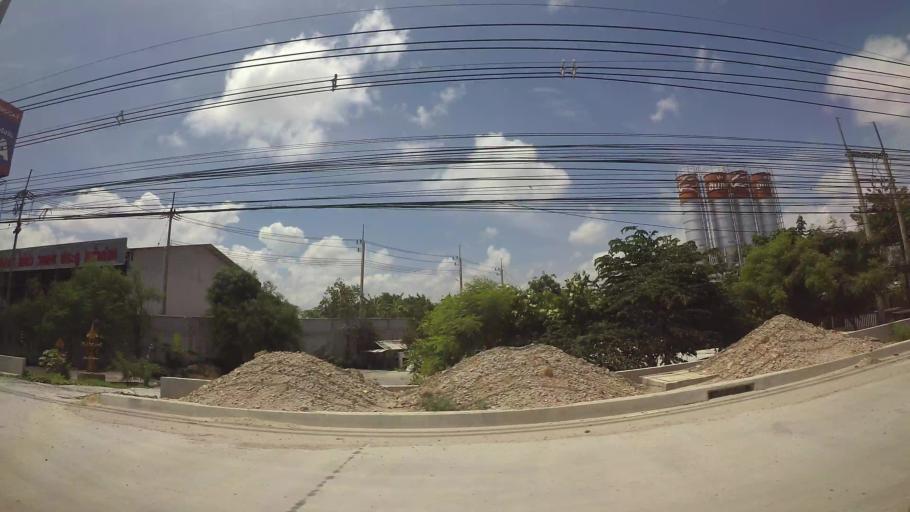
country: TH
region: Rayong
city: Rayong
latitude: 12.7098
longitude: 101.2360
